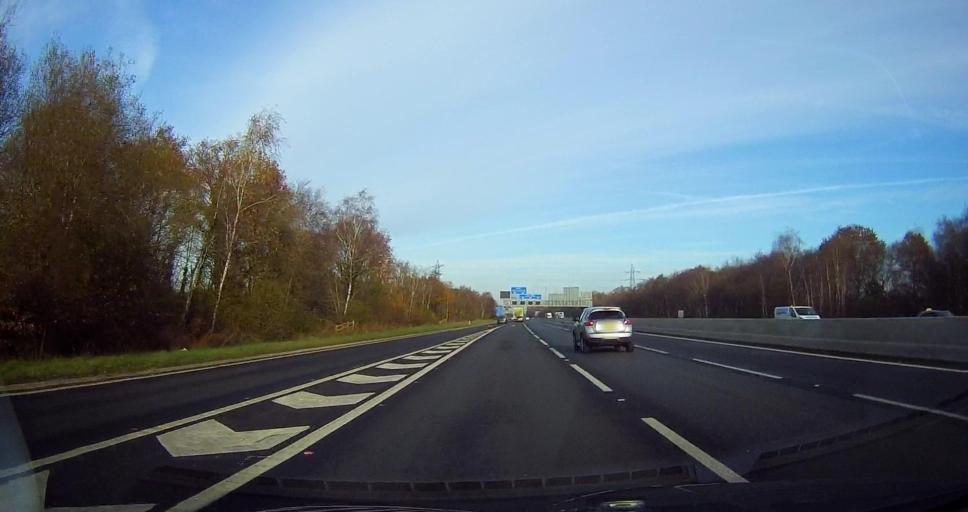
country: GB
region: England
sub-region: West Sussex
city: Copthorne
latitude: 51.1399
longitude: -0.1392
